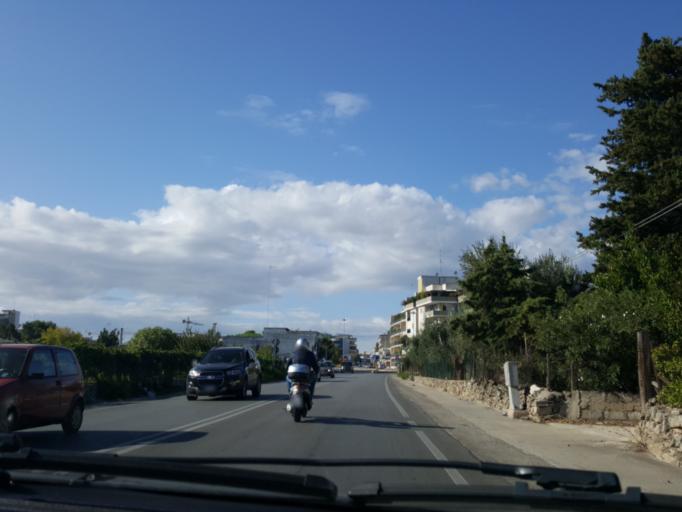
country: IT
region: Apulia
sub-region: Provincia di Bari
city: Triggiano
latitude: 41.0726
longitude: 16.9365
